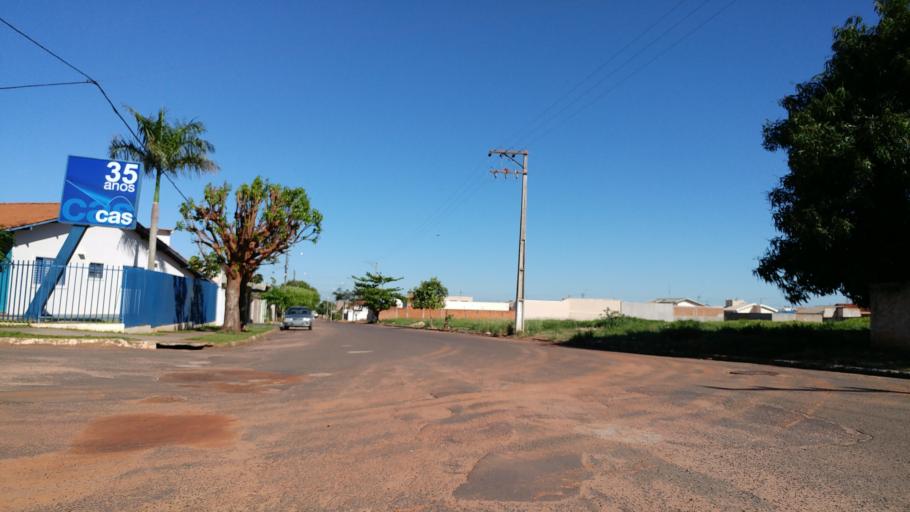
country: BR
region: Sao Paulo
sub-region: Paraguacu Paulista
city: Paraguacu Paulista
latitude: -22.4177
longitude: -50.5884
